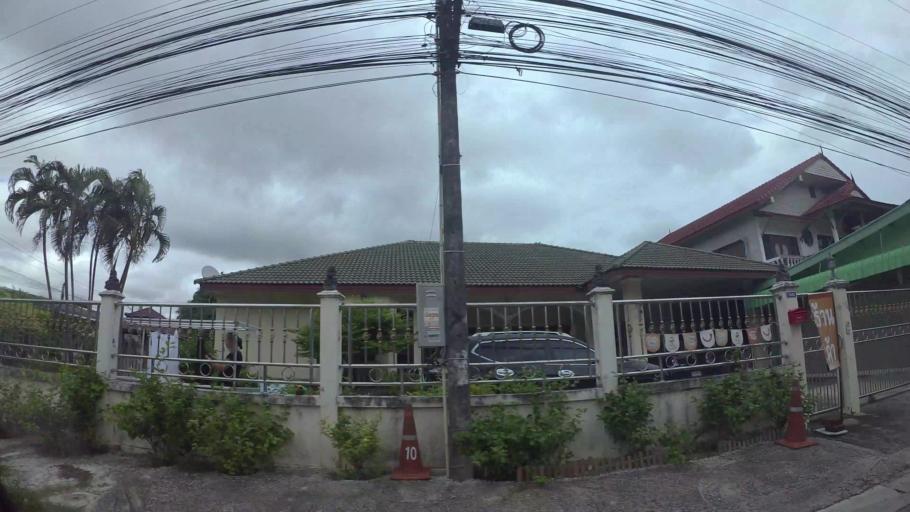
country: TH
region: Rayong
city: Rayong
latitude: 12.6693
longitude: 101.2799
